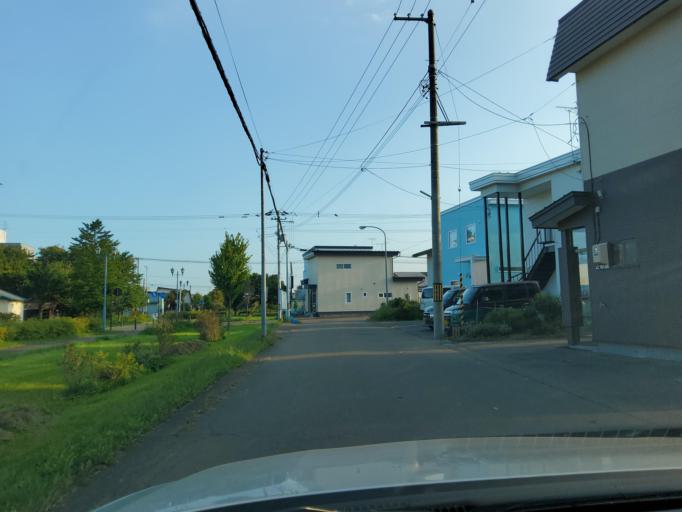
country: JP
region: Hokkaido
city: Obihiro
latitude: 42.9321
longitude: 143.1897
